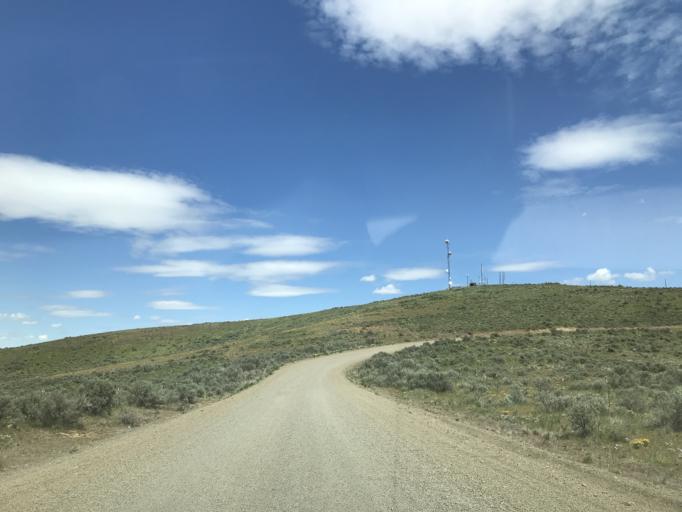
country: US
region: Washington
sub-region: Grant County
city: Quincy
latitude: 47.3182
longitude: -119.8062
